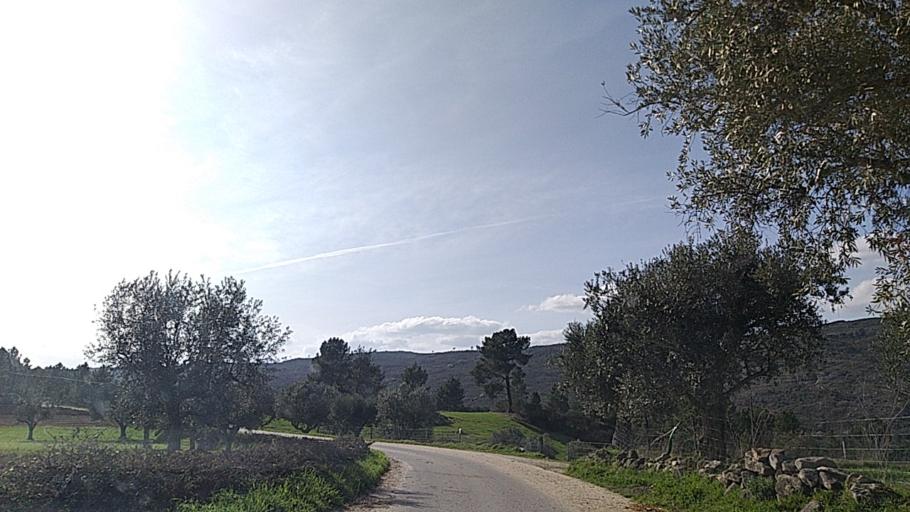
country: PT
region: Guarda
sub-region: Celorico da Beira
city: Celorico da Beira
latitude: 40.6543
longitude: -7.4127
